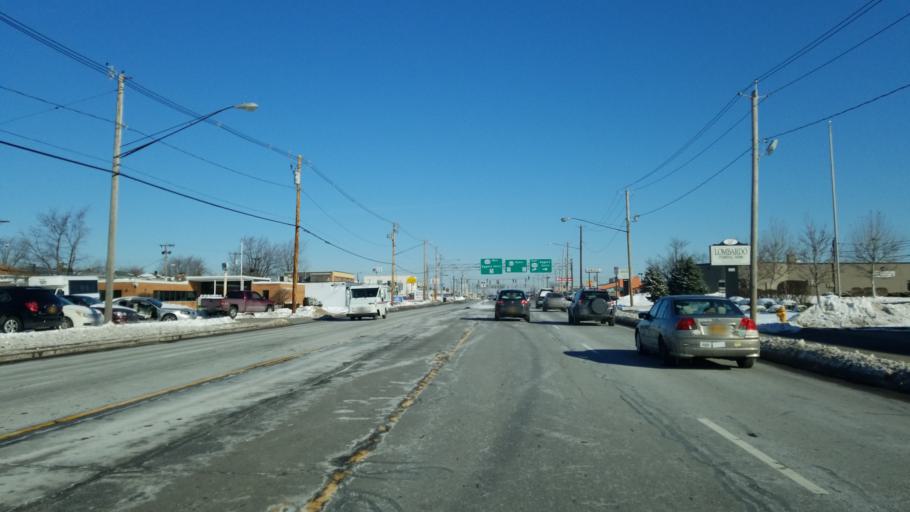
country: US
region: New York
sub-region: Erie County
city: Amherst
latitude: 42.9778
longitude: -78.8230
